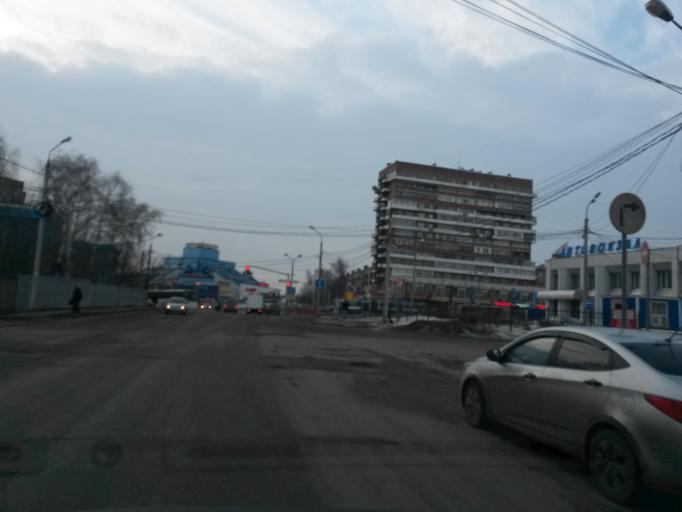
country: RU
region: Jaroslavl
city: Yaroslavl
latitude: 57.5936
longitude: 39.8622
